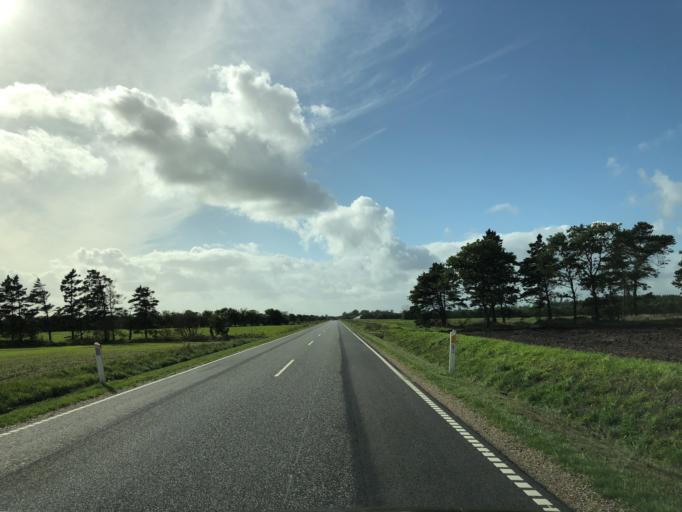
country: DK
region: Central Jutland
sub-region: Holstebro Kommune
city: Holstebro
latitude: 56.3688
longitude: 8.4680
